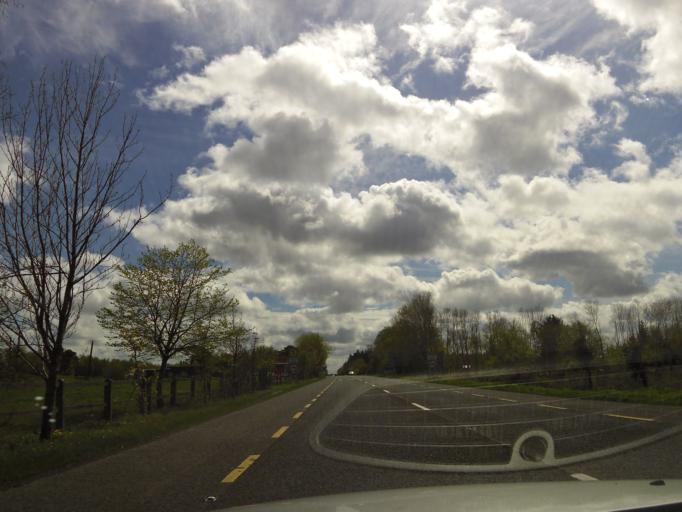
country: IE
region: Connaught
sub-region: Maigh Eo
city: Claremorris
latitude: 53.7041
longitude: -8.9815
